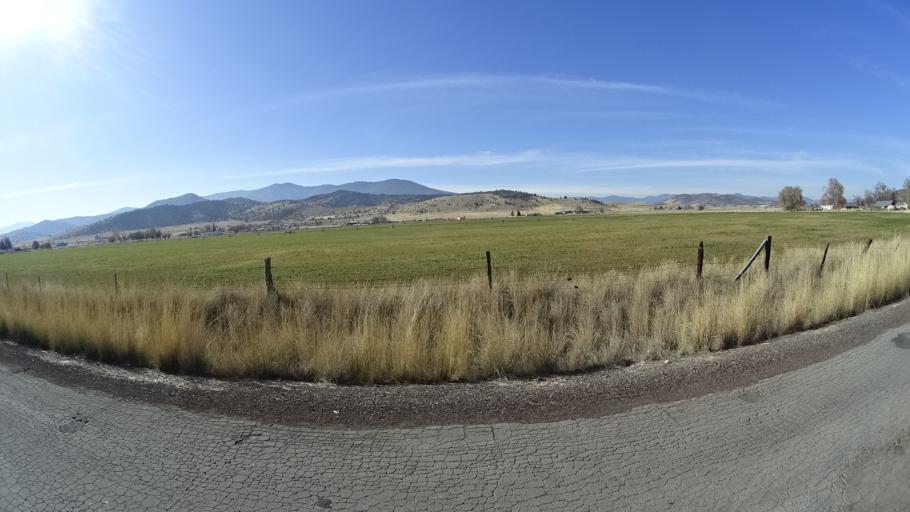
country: US
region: California
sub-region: Siskiyou County
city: Montague
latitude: 41.6377
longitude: -122.5216
